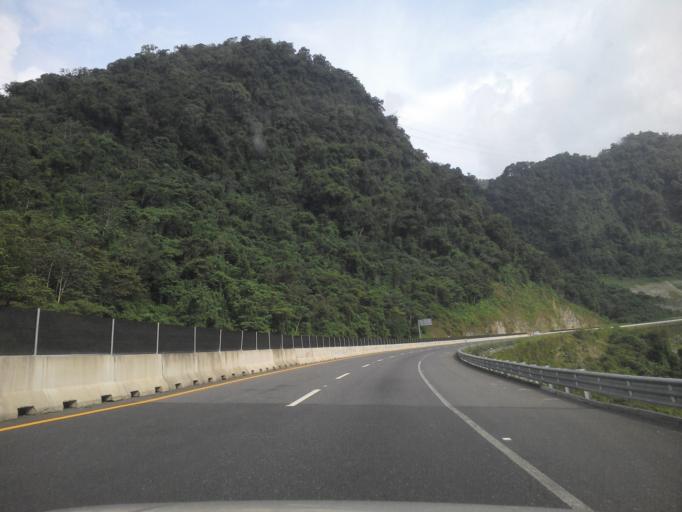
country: MX
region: Puebla
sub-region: Xicotepec
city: San Lorenzo
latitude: 20.3375
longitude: -97.9588
